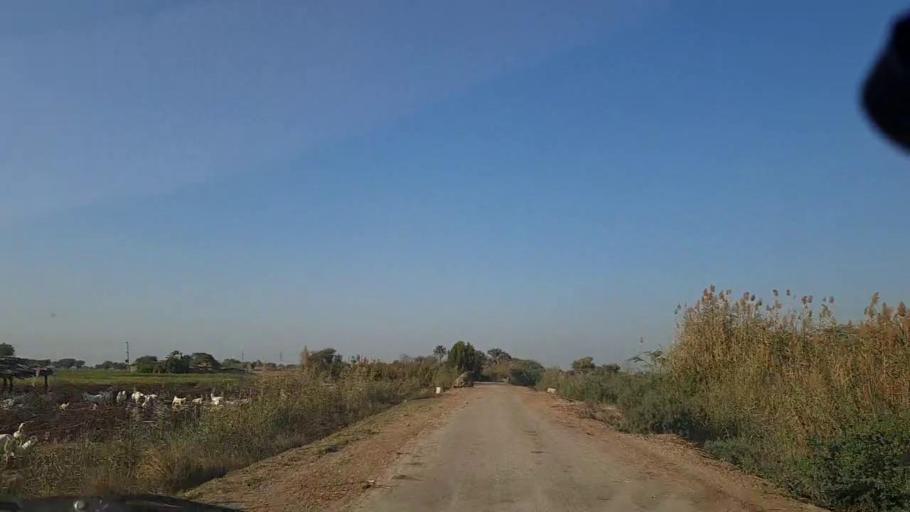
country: PK
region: Sindh
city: Berani
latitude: 25.6723
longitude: 68.9149
